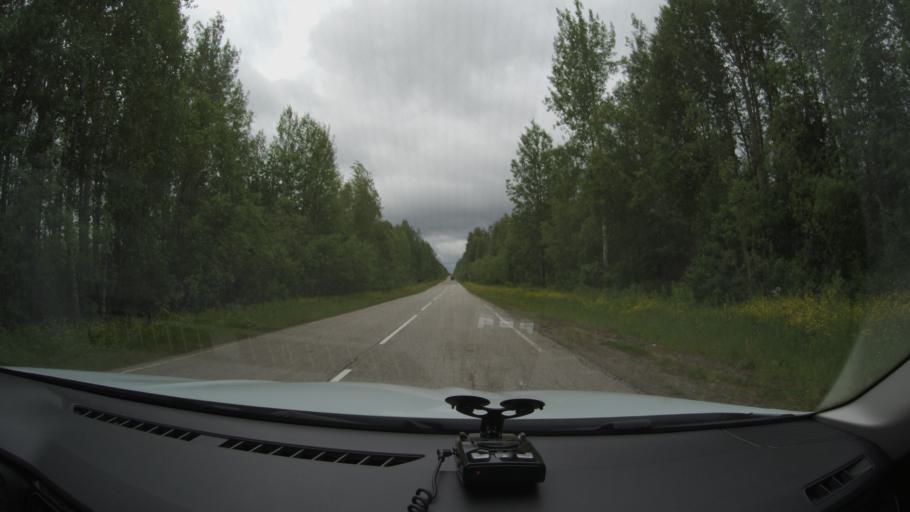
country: RU
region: Komi Republic
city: Nizhniy Odes
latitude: 63.6054
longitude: 54.5434
